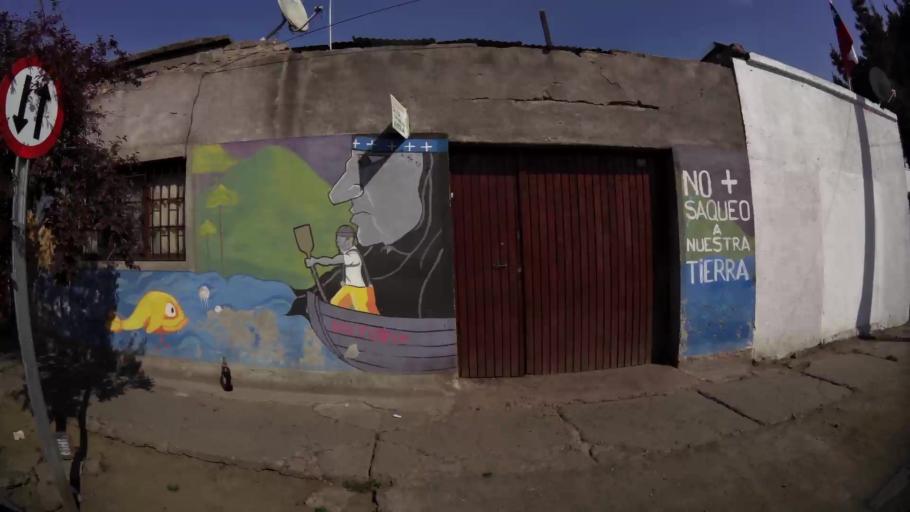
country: CL
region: Santiago Metropolitan
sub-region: Provincia de Santiago
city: Lo Prado
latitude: -33.4246
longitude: -70.7244
